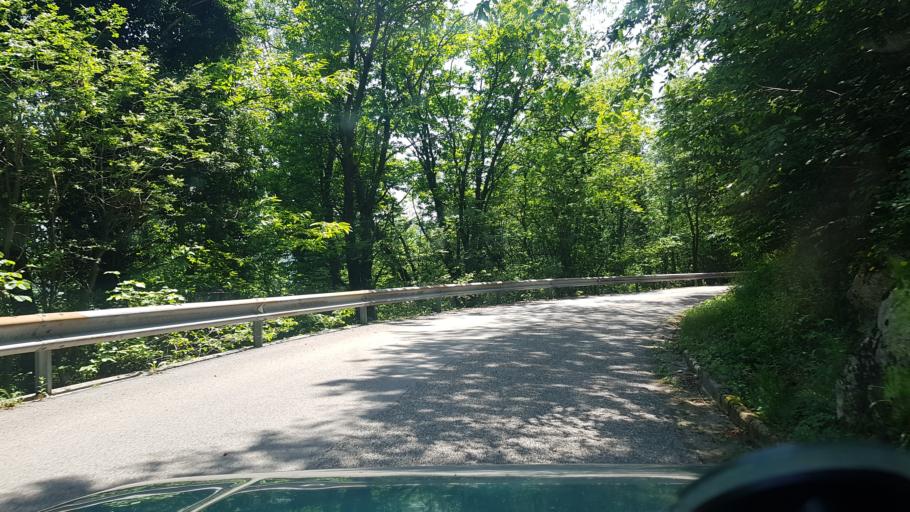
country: IT
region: Friuli Venezia Giulia
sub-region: Provincia di Udine
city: Lusevera
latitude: 46.2760
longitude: 13.2965
